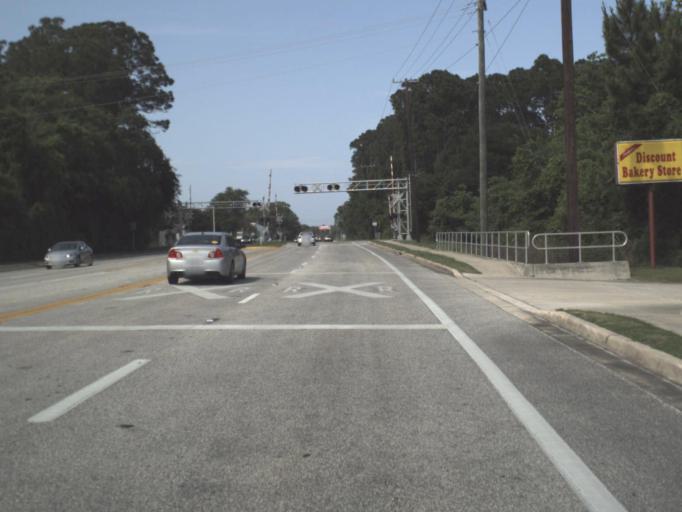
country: US
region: Florida
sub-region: Saint Johns County
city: Saint Augustine
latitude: 29.8716
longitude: -81.3348
